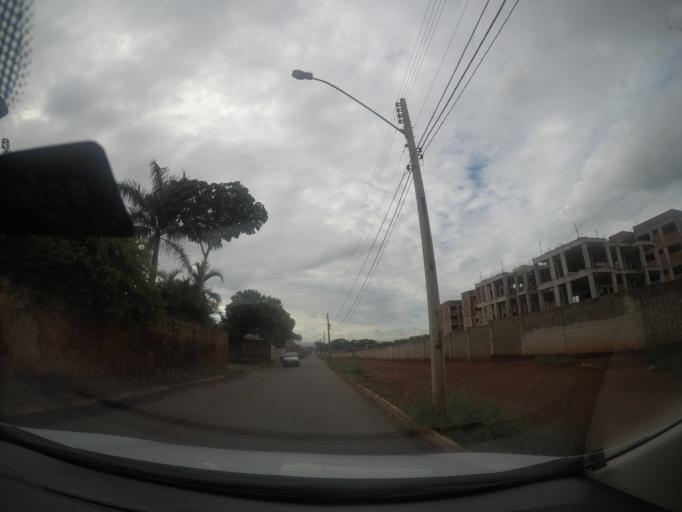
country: BR
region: Goias
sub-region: Goiania
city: Goiania
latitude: -16.6131
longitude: -49.3326
